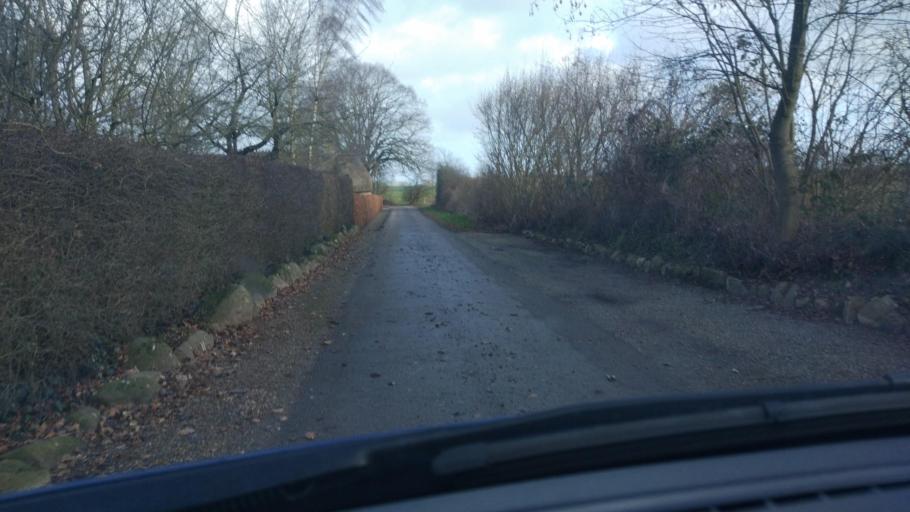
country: DE
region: Schleswig-Holstein
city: Taarstedt
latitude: 54.5585
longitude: 9.6846
